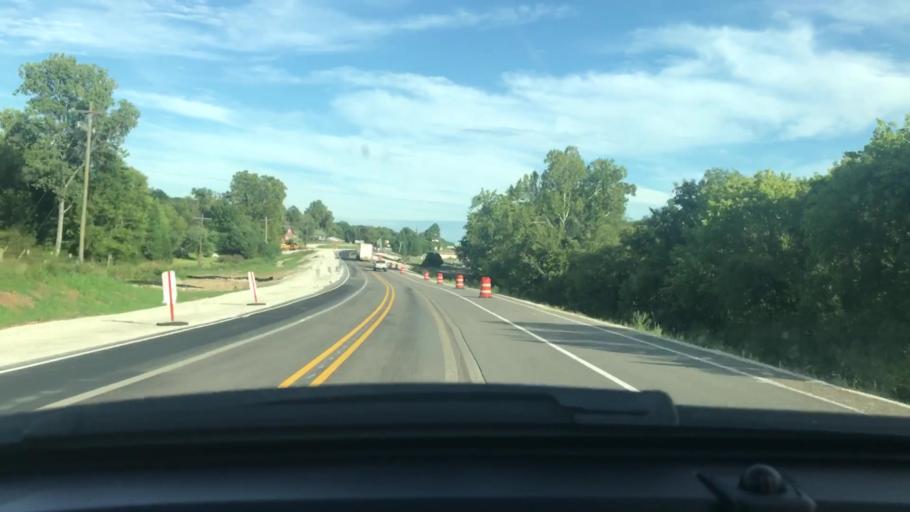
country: US
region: Arkansas
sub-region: Sharp County
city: Cherokee Village
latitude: 36.3042
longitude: -91.4493
